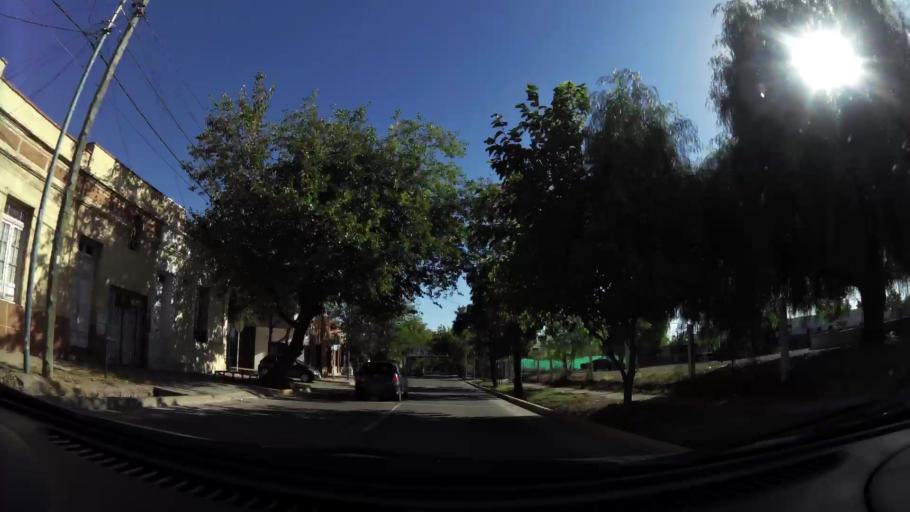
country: AR
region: Mendoza
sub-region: Departamento de Godoy Cruz
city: Godoy Cruz
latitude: -32.9193
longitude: -68.8435
